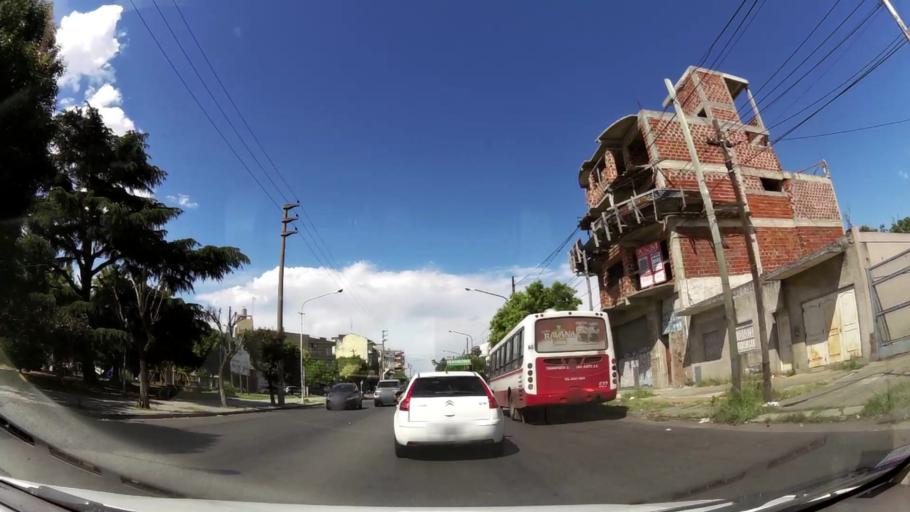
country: AR
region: Buenos Aires
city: San Justo
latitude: -34.6669
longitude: -58.5502
